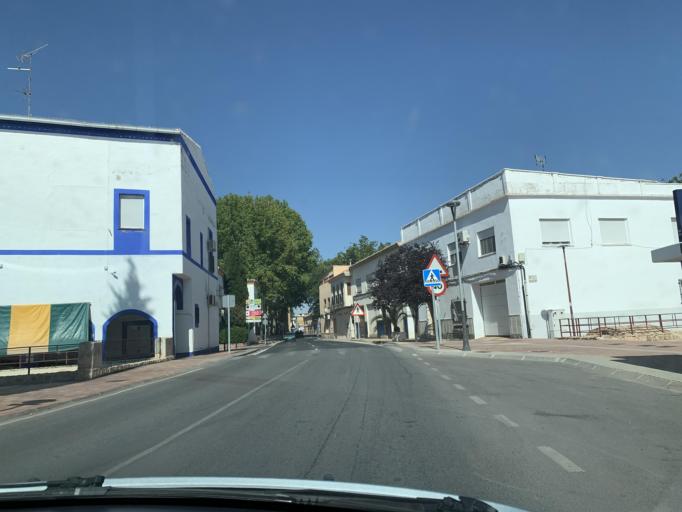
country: ES
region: Castille-La Mancha
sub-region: Provincia de Ciudad Real
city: Argamasilla de Alba
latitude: 39.1283
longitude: -3.0908
